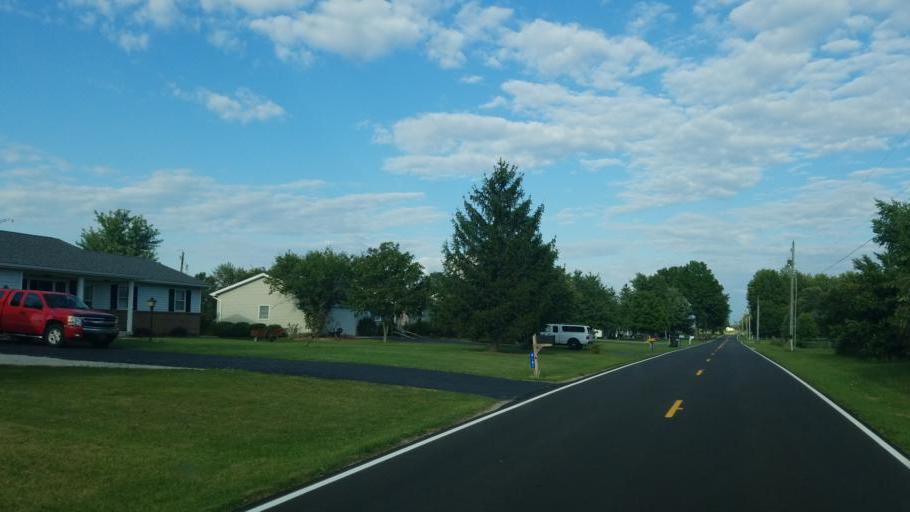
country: US
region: Ohio
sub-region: Seneca County
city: Tiffin
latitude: 41.1100
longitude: -83.0879
